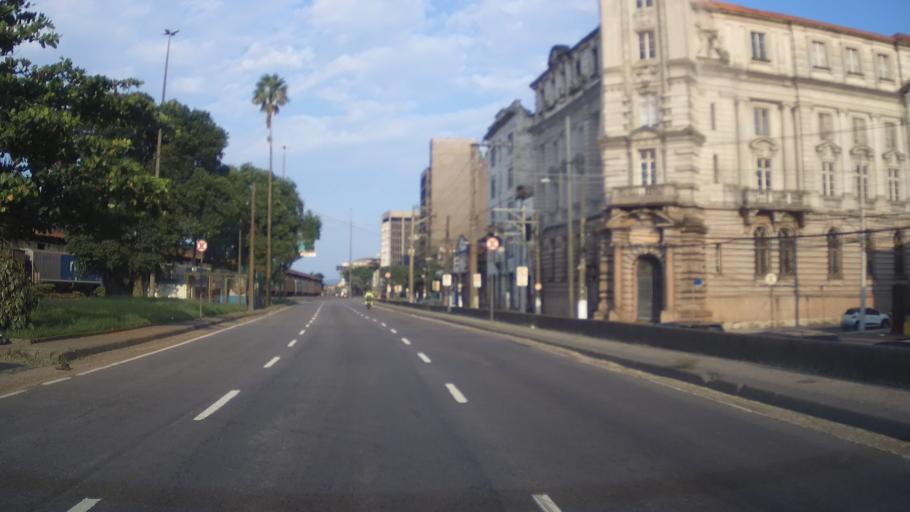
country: BR
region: Sao Paulo
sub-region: Santos
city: Santos
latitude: -23.9316
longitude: -46.3306
